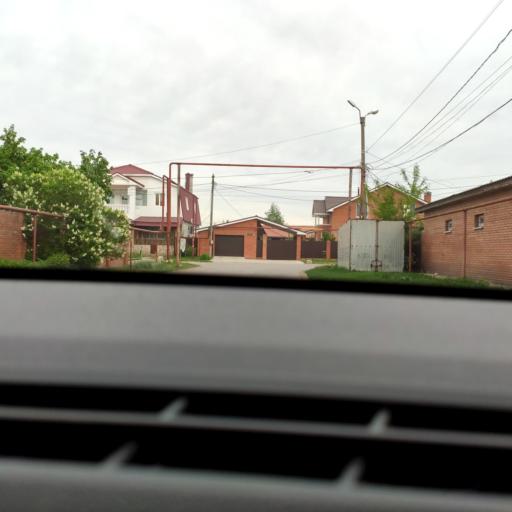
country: RU
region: Samara
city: Tol'yatti
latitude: 53.5618
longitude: 49.3800
